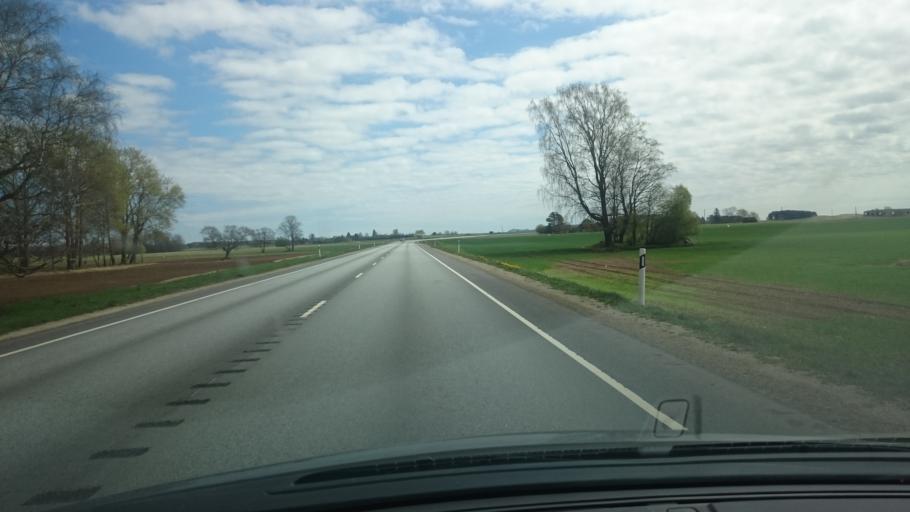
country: EE
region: Ida-Virumaa
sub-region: Puessi linn
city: Pussi
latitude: 59.4120
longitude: 27.0347
